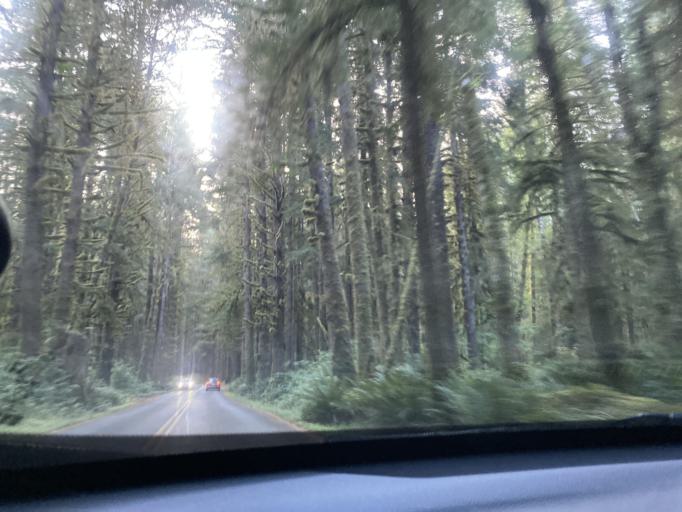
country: US
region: Washington
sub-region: Clallam County
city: Forks
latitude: 47.8156
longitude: -124.0617
